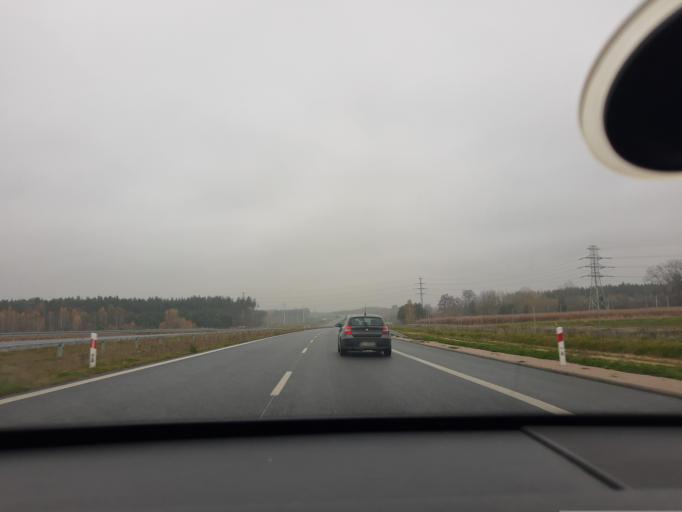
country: PL
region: Lodz Voivodeship
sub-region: Powiat pabianicki
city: Konstantynow Lodzki
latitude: 51.7097
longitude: 19.3444
